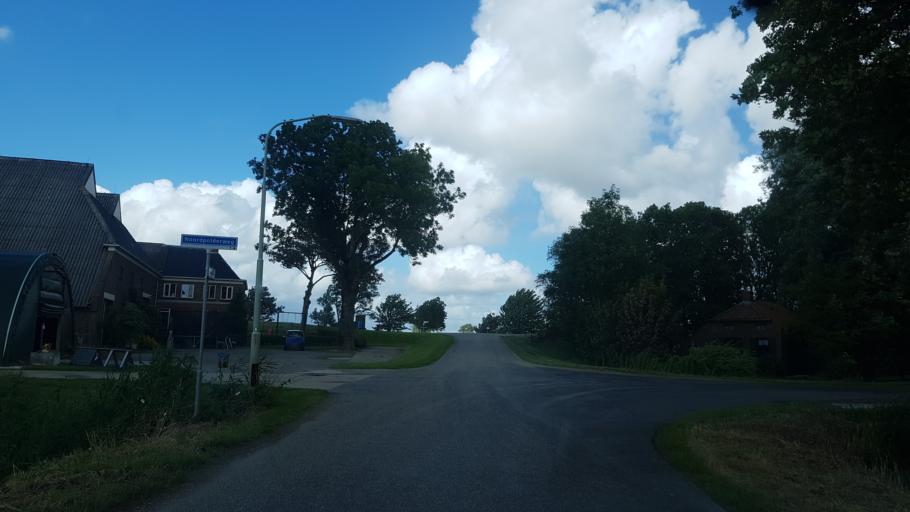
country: NL
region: Groningen
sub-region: Gemeente Winsum
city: Winsum
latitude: 53.4148
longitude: 6.4855
